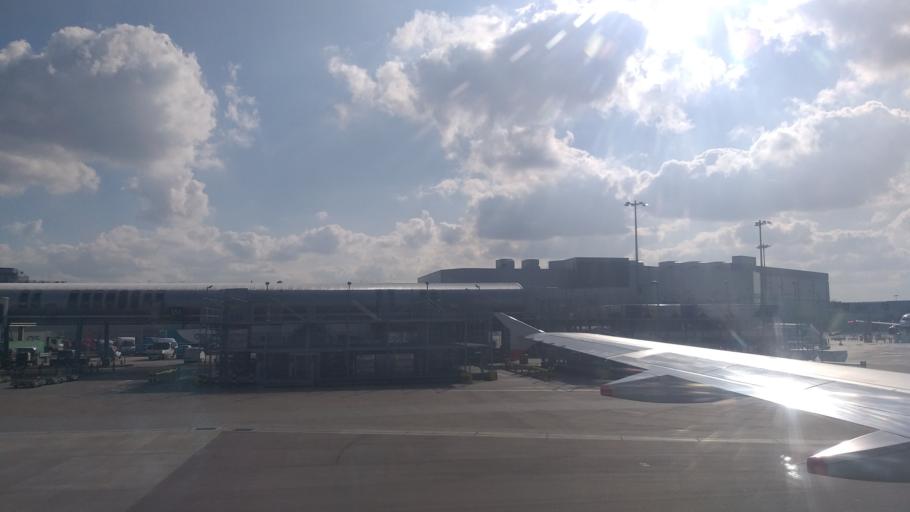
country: GB
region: England
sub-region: Greater London
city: West Drayton
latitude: 51.4751
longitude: -0.4572
